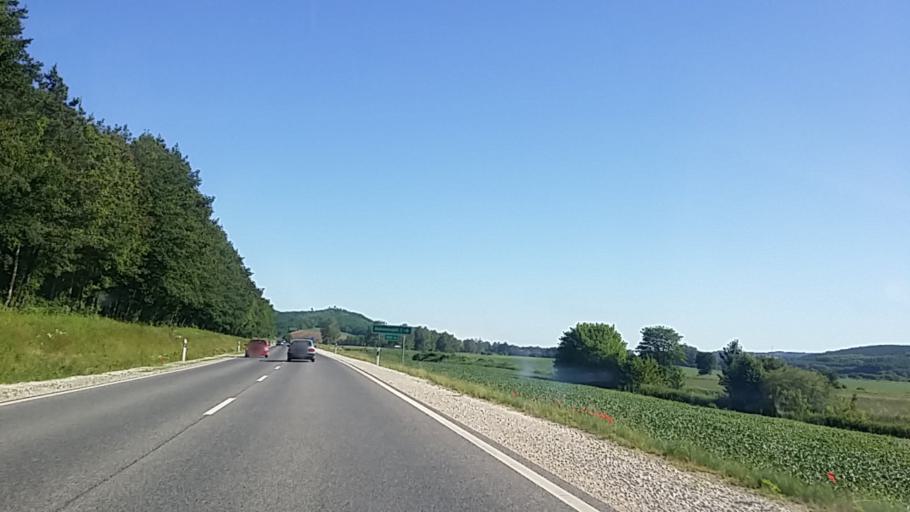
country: HU
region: Zala
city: Zalaegerszeg
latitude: 46.8331
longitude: 16.9288
